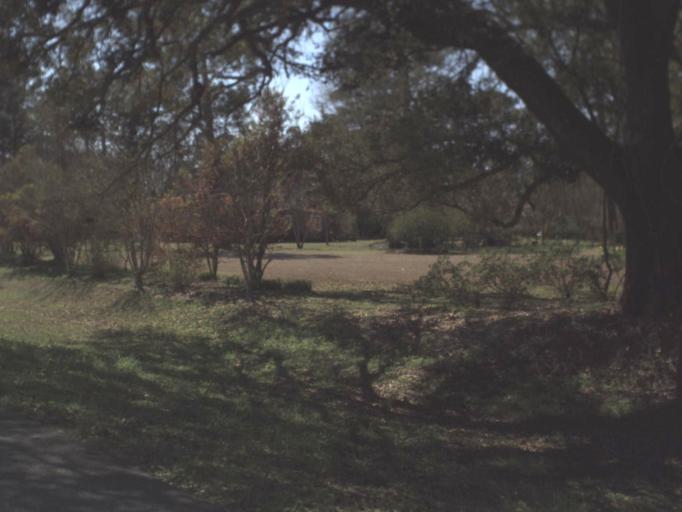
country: US
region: Florida
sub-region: Calhoun County
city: Blountstown
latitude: 30.5669
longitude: -85.0218
